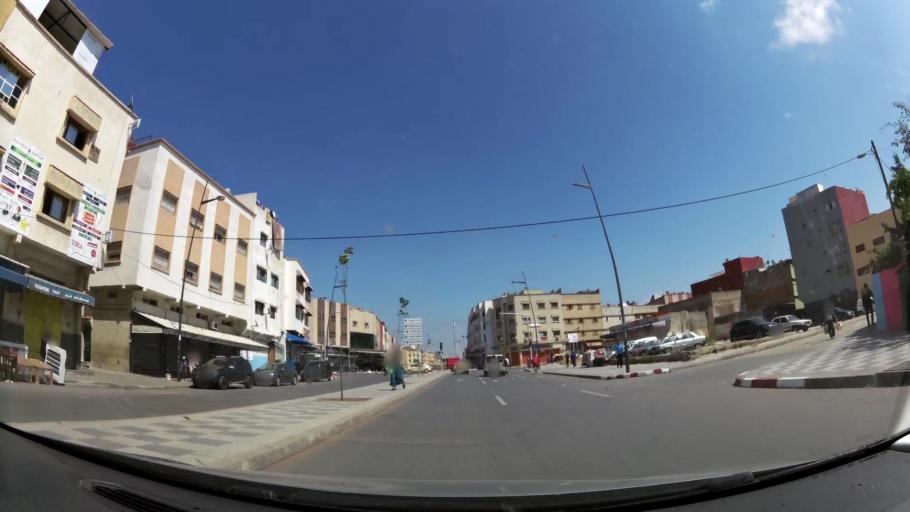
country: MA
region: Rabat-Sale-Zemmour-Zaer
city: Sale
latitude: 34.0579
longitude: -6.7781
